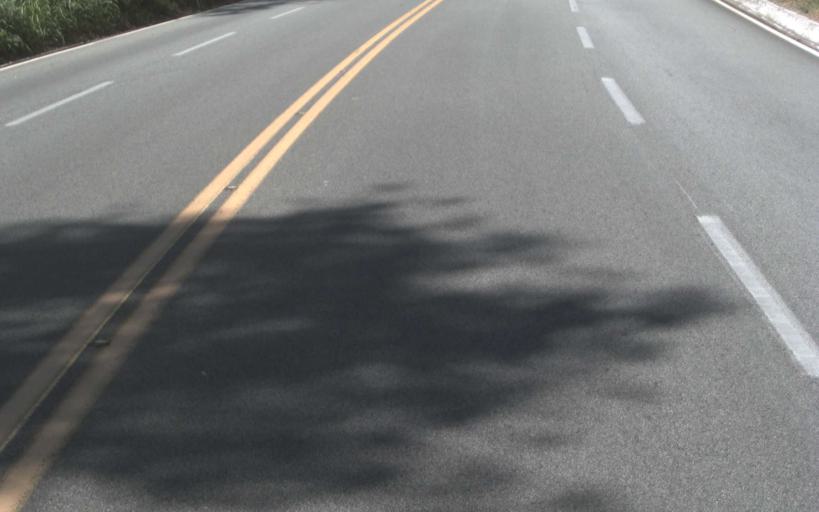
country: BR
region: Minas Gerais
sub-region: Joao Monlevade
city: Joao Monlevade
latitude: -19.8441
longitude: -43.1045
